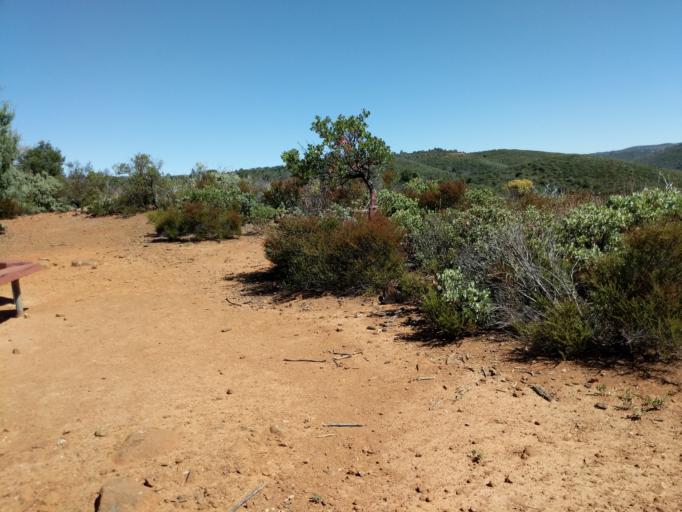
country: US
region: California
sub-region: San Diego County
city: Julian
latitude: 33.0352
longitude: -116.6301
